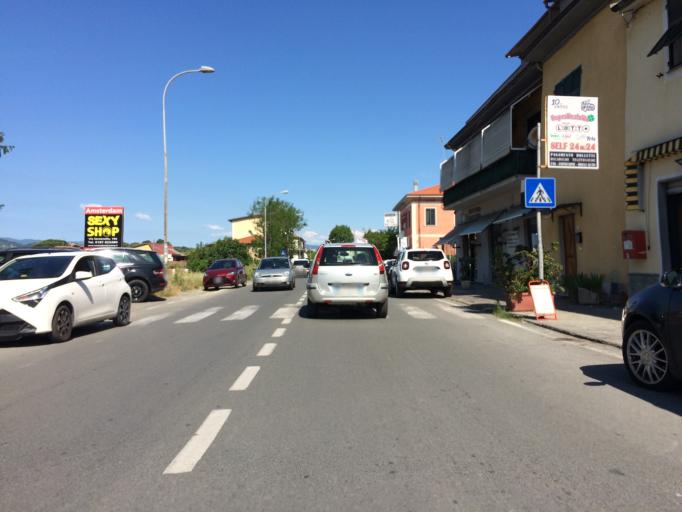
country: IT
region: Tuscany
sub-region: Provincia di Massa-Carrara
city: Borghetto-Melara
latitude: 44.0952
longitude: 9.9900
